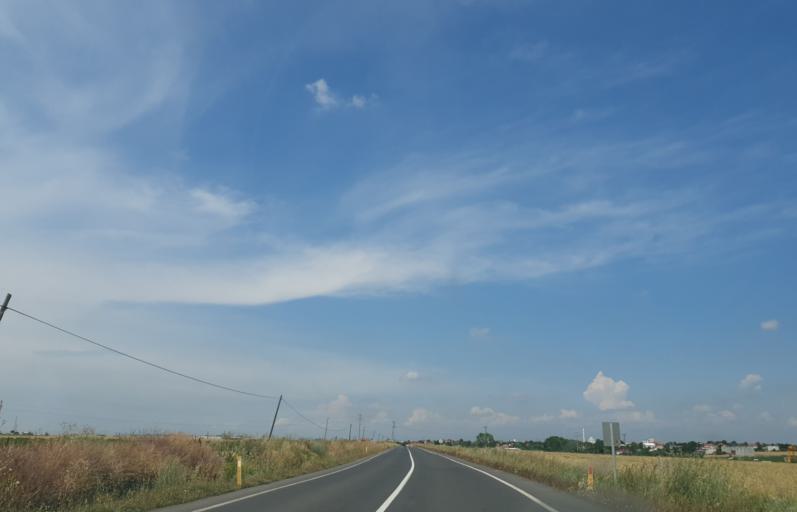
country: TR
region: Kirklareli
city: Buyukkaristiran
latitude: 41.2542
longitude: 27.6269
